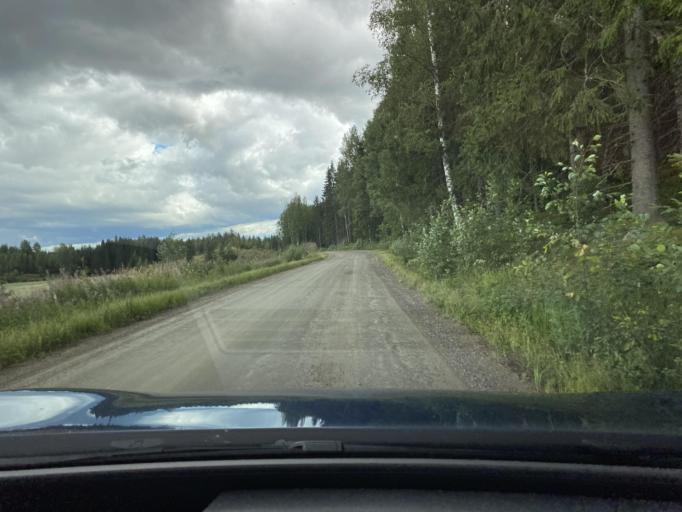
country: FI
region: Pirkanmaa
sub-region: Lounais-Pirkanmaa
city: Punkalaidun
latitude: 61.2264
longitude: 23.1553
